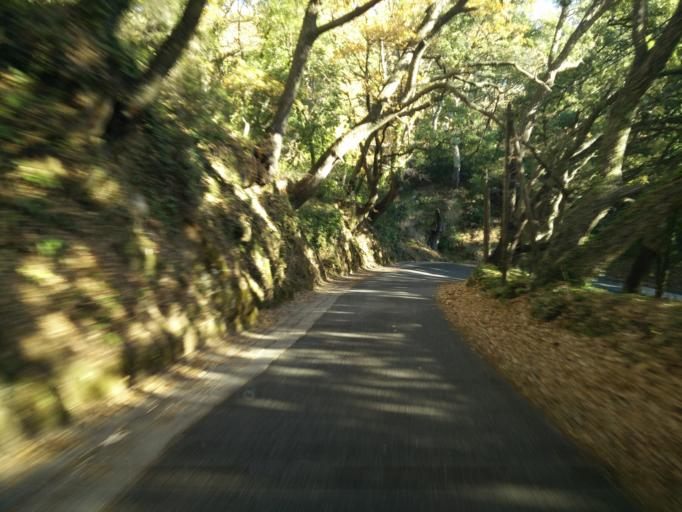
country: FR
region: Provence-Alpes-Cote d'Azur
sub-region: Departement du Var
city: La Garde-Freinet
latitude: 43.3114
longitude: 6.4755
